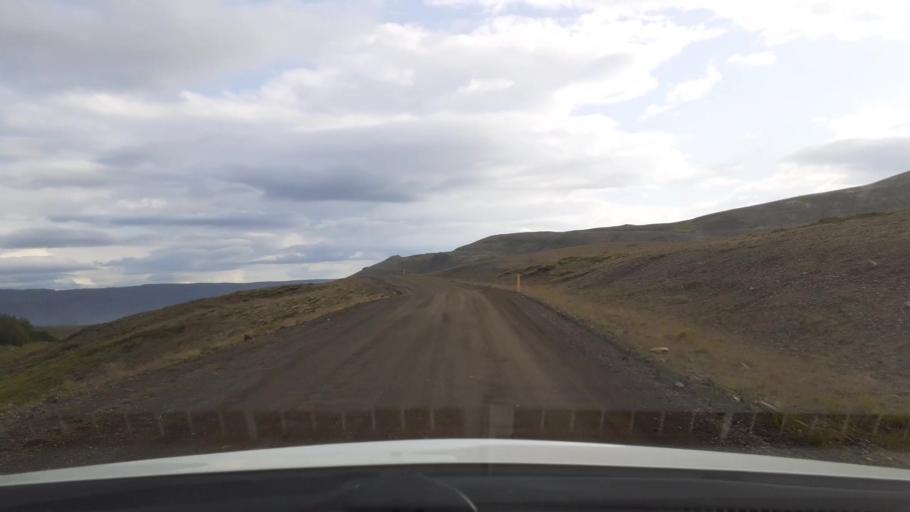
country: IS
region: Capital Region
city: Mosfellsbaer
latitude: 64.2952
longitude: -21.6588
